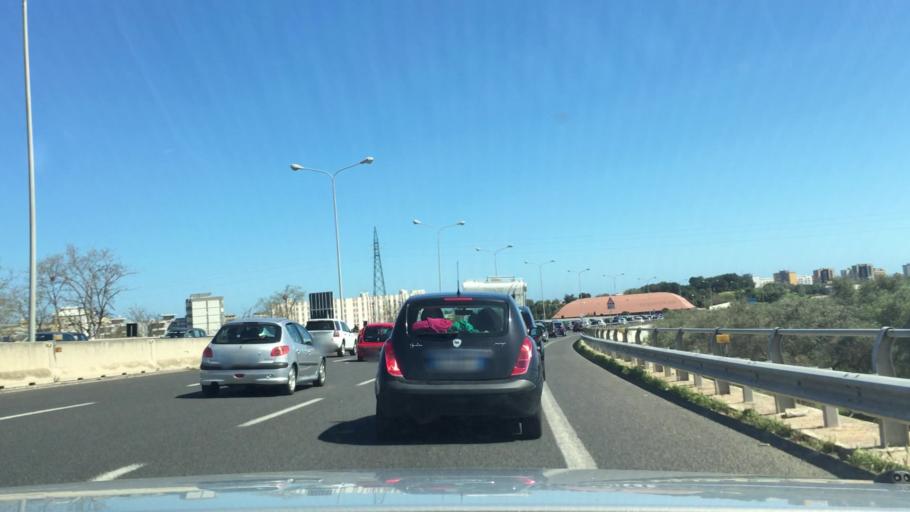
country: IT
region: Apulia
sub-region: Provincia di Bari
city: Triggiano
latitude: 41.0961
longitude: 16.8988
